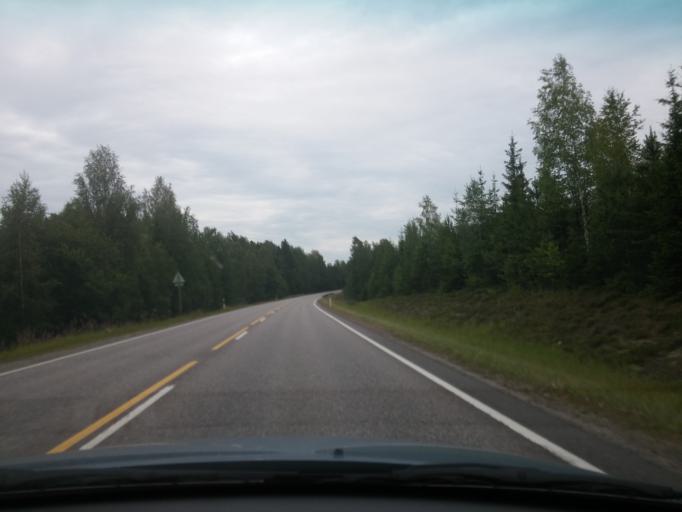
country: FI
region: Haeme
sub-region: Riihimaeki
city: Loppi
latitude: 60.7310
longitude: 24.3954
